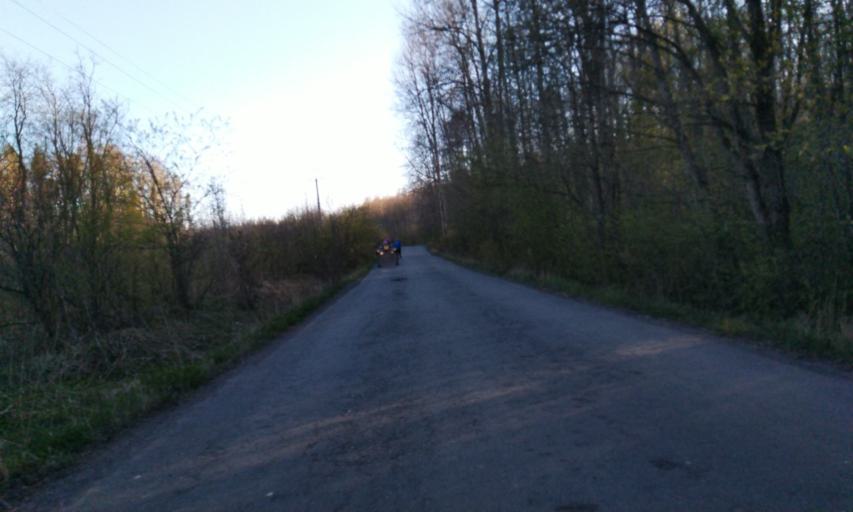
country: RU
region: Leningrad
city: Toksovo
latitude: 60.1438
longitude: 30.5736
